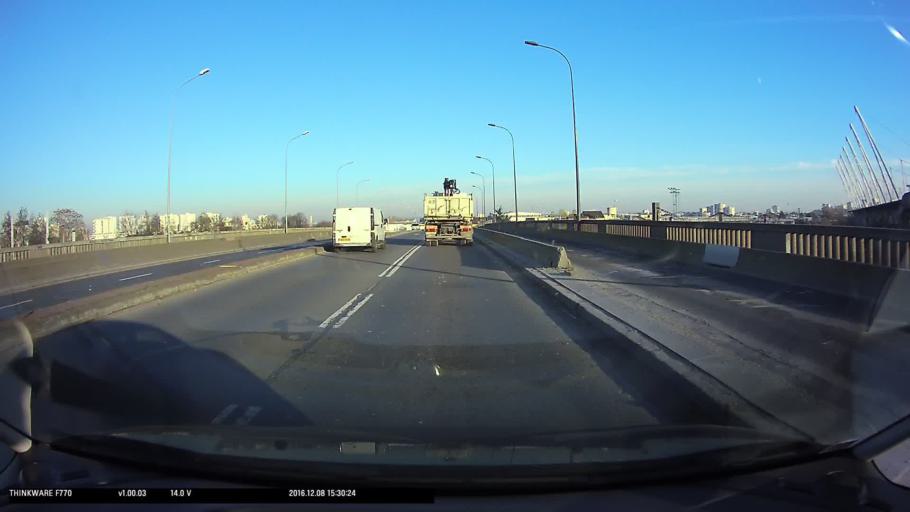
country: FR
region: Ile-de-France
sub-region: Departement de Seine-Saint-Denis
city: Bobigny
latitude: 48.8977
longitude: 2.4377
